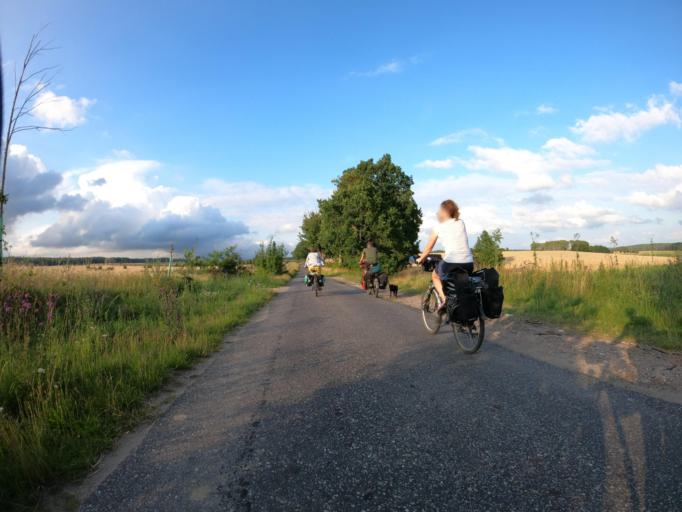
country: PL
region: West Pomeranian Voivodeship
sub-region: Powiat szczecinecki
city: Borne Sulinowo
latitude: 53.6986
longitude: 16.5075
